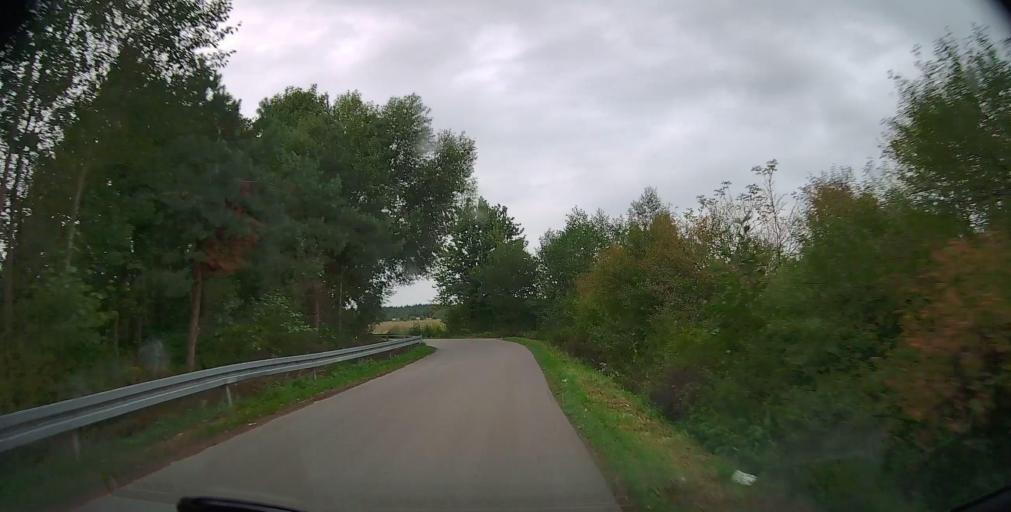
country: PL
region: Masovian Voivodeship
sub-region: Powiat radomski
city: Jedlinsk
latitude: 51.4551
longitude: 21.1038
